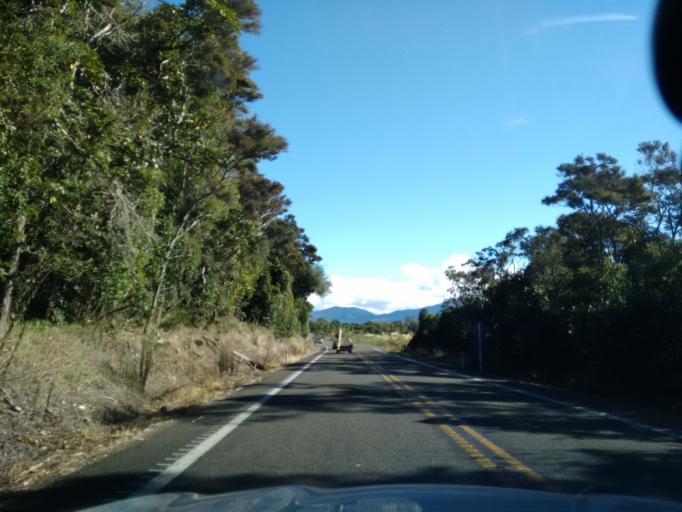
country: NZ
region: Waikato
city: Turangi
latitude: -38.9417
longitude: 175.8573
